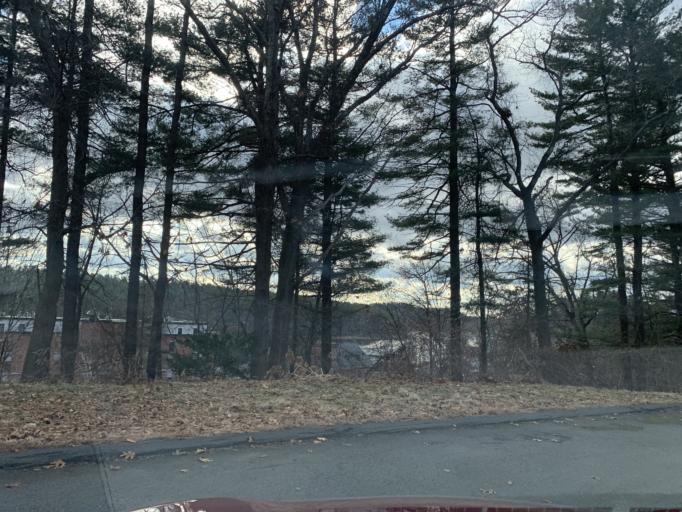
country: US
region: Massachusetts
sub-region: Essex County
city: Amesbury
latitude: 42.8377
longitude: -70.9297
